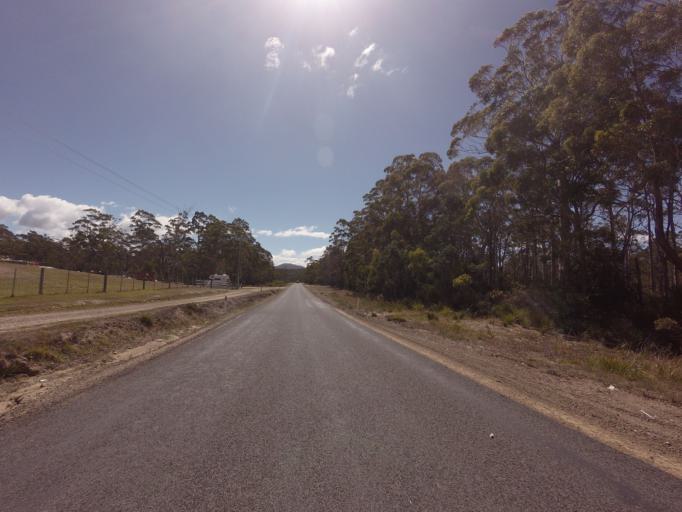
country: AU
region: Tasmania
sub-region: Break O'Day
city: St Helens
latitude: -41.5989
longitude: 148.2043
